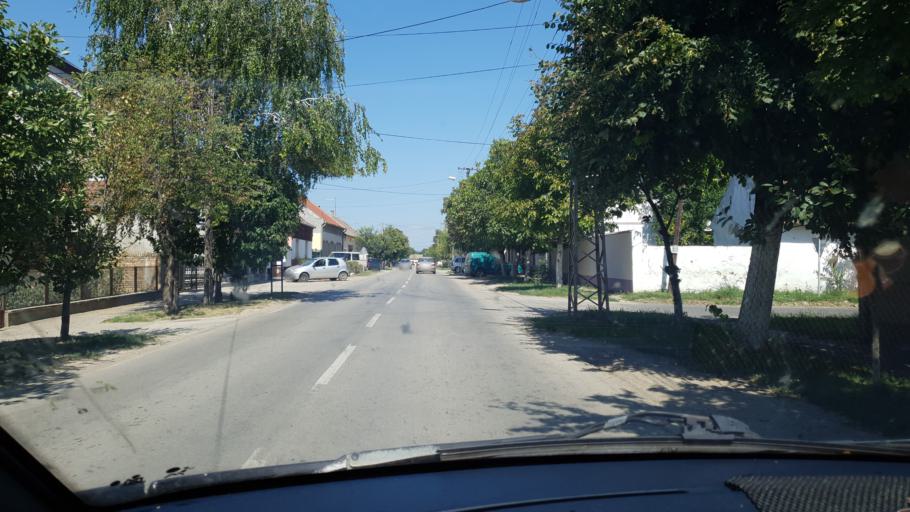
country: RS
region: Autonomna Pokrajina Vojvodina
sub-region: Juznobacki Okrug
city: Kovilj
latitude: 45.2304
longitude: 20.0229
